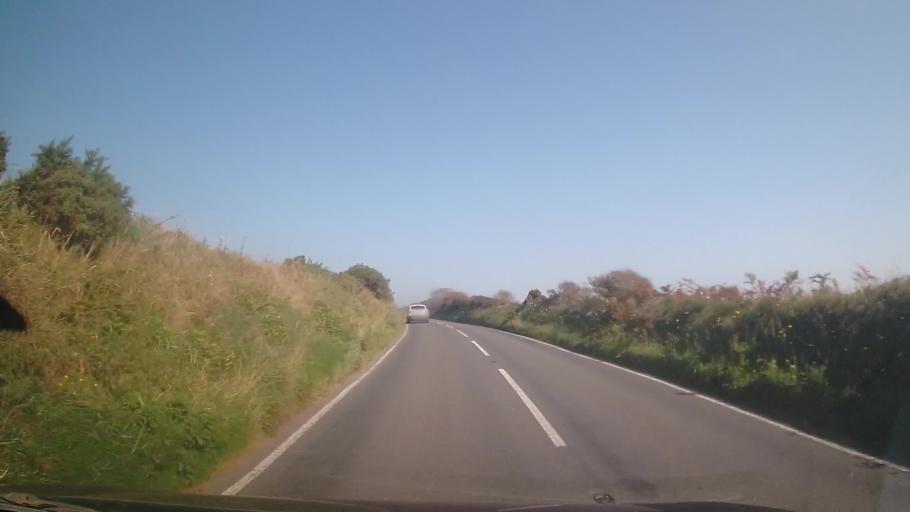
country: GB
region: Wales
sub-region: Pembrokeshire
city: Llanrhian
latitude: 51.9027
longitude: -5.2073
